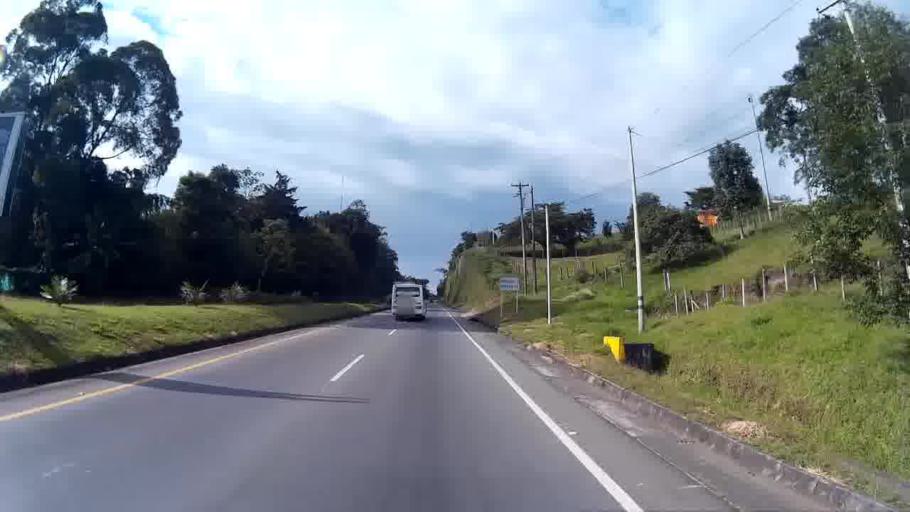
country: CO
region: Quindio
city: Circasia
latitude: 4.5997
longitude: -75.6373
